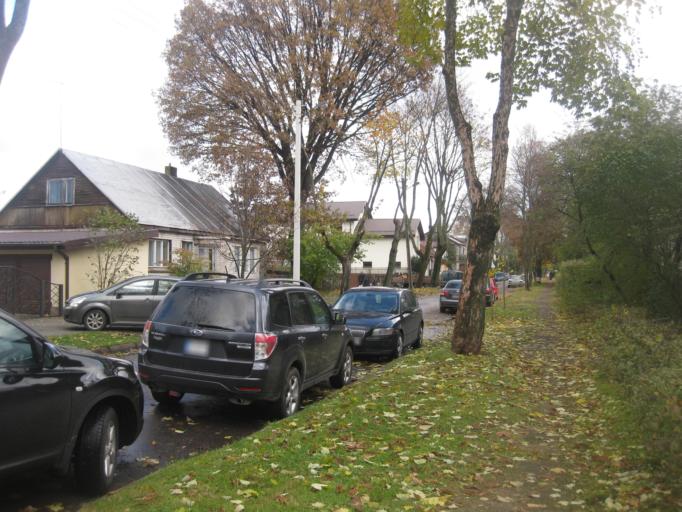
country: LT
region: Kauno apskritis
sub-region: Kaunas
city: Eiguliai
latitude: 54.9046
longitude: 23.9349
